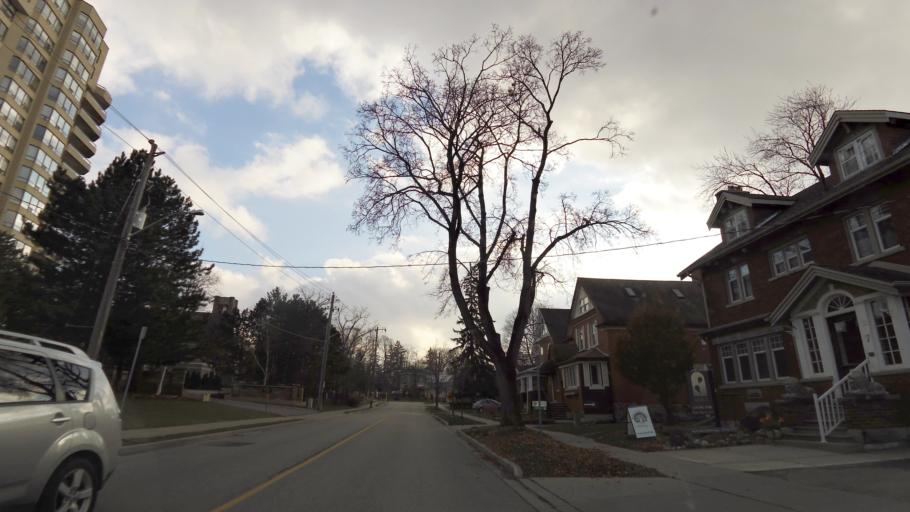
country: CA
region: Ontario
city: Waterloo
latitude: 43.4656
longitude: -80.5180
